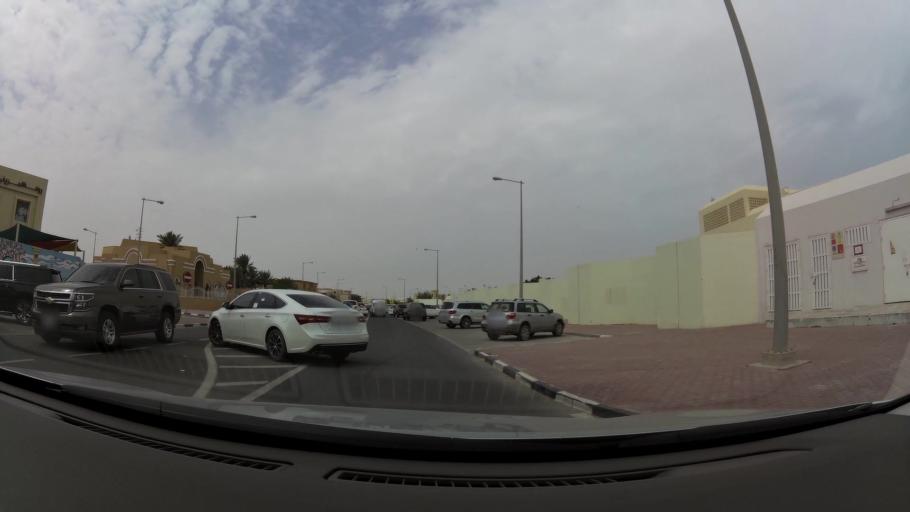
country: QA
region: Baladiyat ar Rayyan
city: Ar Rayyan
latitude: 25.3296
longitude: 51.4773
